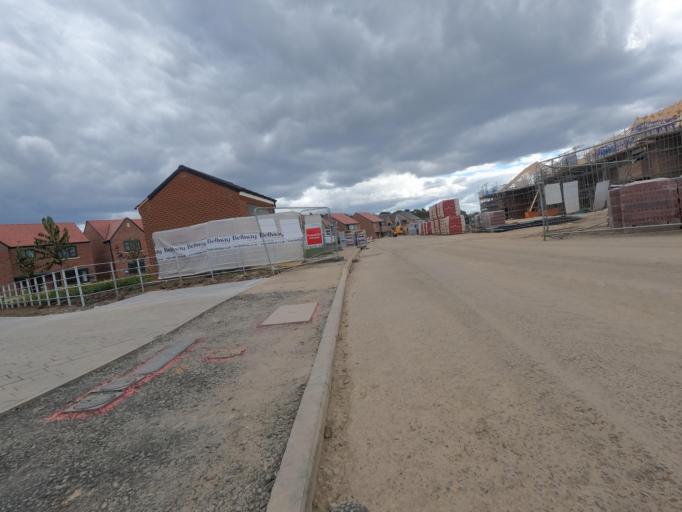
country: GB
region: England
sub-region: Northumberland
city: Seghill
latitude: 55.0363
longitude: -1.5864
